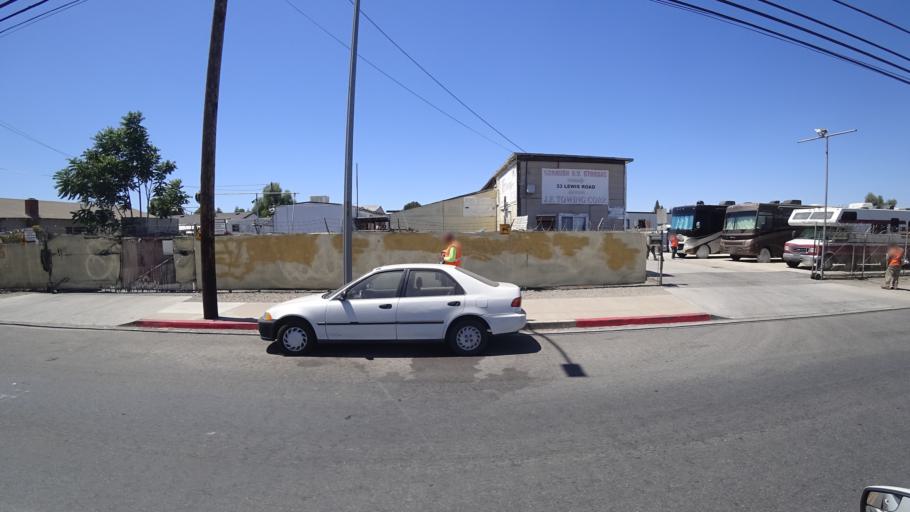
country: US
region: California
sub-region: Santa Clara County
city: Seven Trees
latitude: 37.2910
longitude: -121.8472
